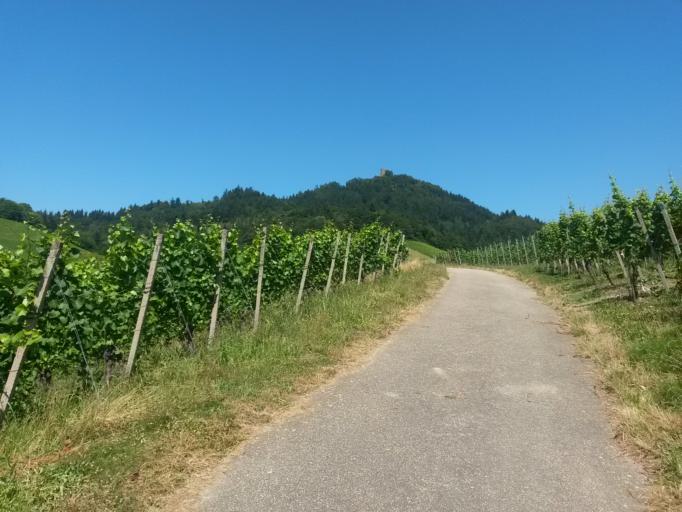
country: DE
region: Baden-Wuerttemberg
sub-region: Karlsruhe Region
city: Buhlertal
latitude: 48.7228
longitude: 8.1887
